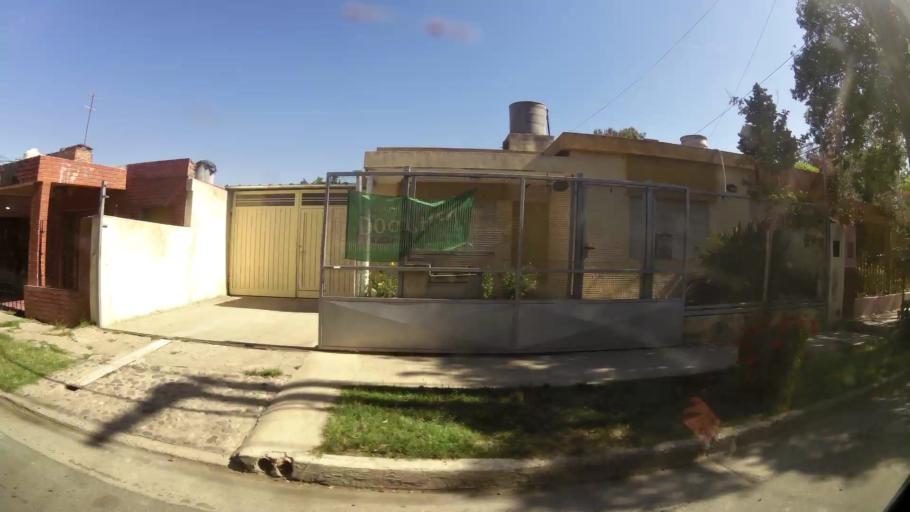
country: AR
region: Cordoba
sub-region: Departamento de Capital
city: Cordoba
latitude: -31.3650
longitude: -64.1740
